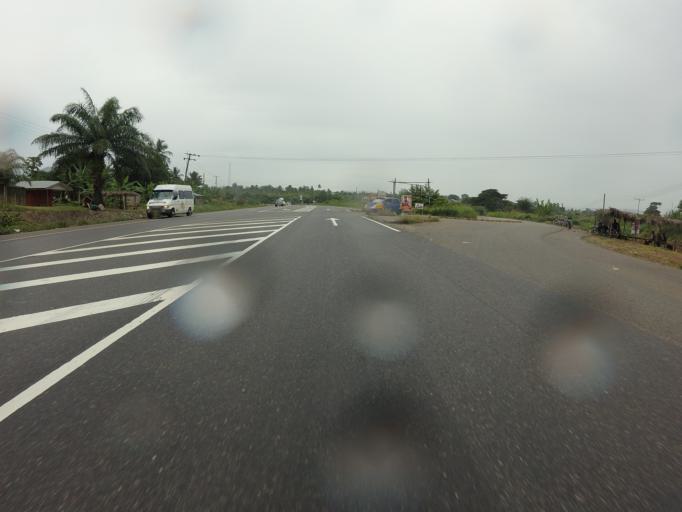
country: GH
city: Kibi
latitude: 6.1712
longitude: -0.4753
